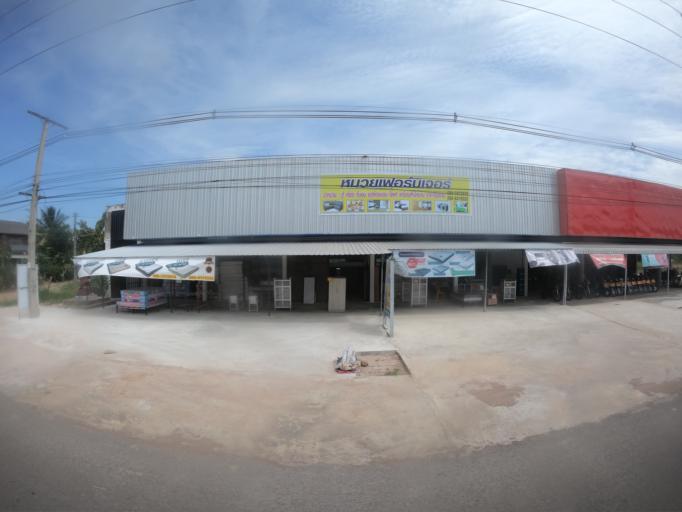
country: TH
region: Maha Sarakham
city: Chiang Yuen
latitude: 16.4177
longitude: 103.0800
